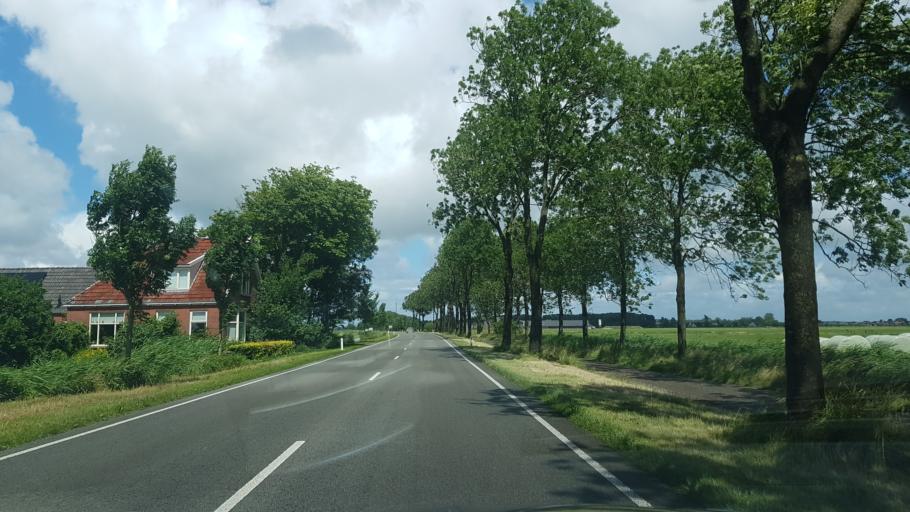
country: NL
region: Groningen
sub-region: Gemeente Winsum
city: Winsum
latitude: 53.3478
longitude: 6.5065
